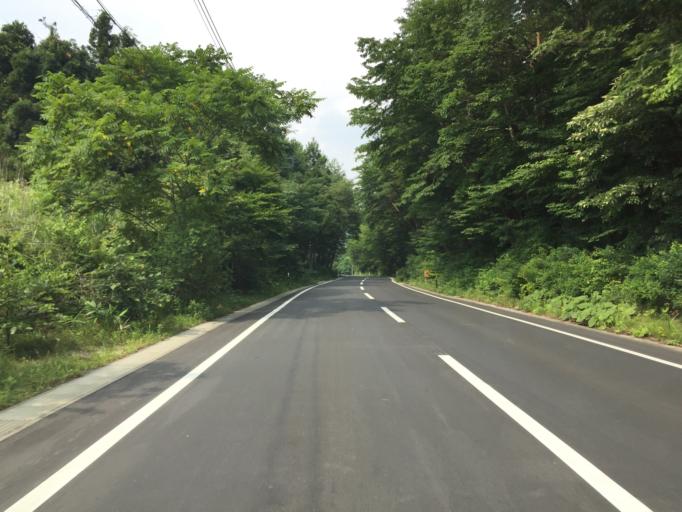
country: JP
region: Fukushima
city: Funehikimachi-funehiki
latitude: 37.4831
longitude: 140.7624
